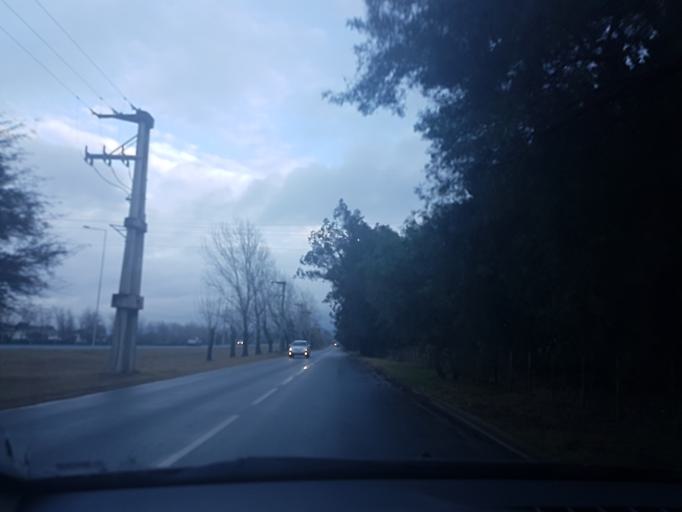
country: AR
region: Cordoba
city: Villa Allende
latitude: -31.3021
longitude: -64.2500
